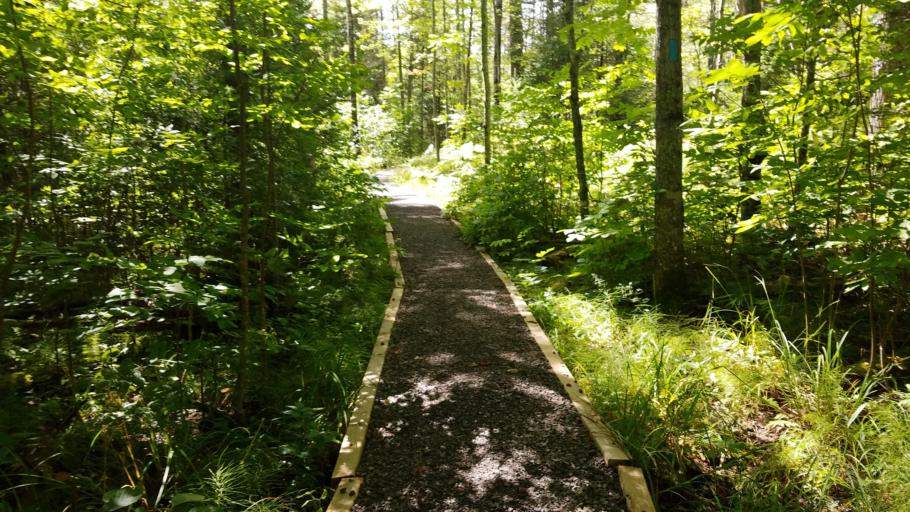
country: US
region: Michigan
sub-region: Ontonagon County
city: Ontonagon
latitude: 46.6485
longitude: -89.1738
